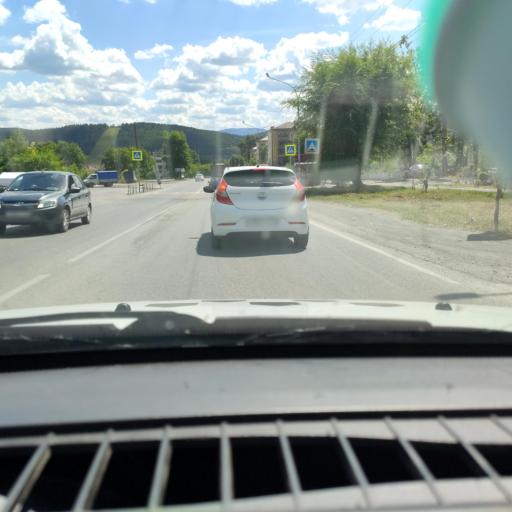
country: RU
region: Chelyabinsk
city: Satka
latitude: 55.0387
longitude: 58.9818
